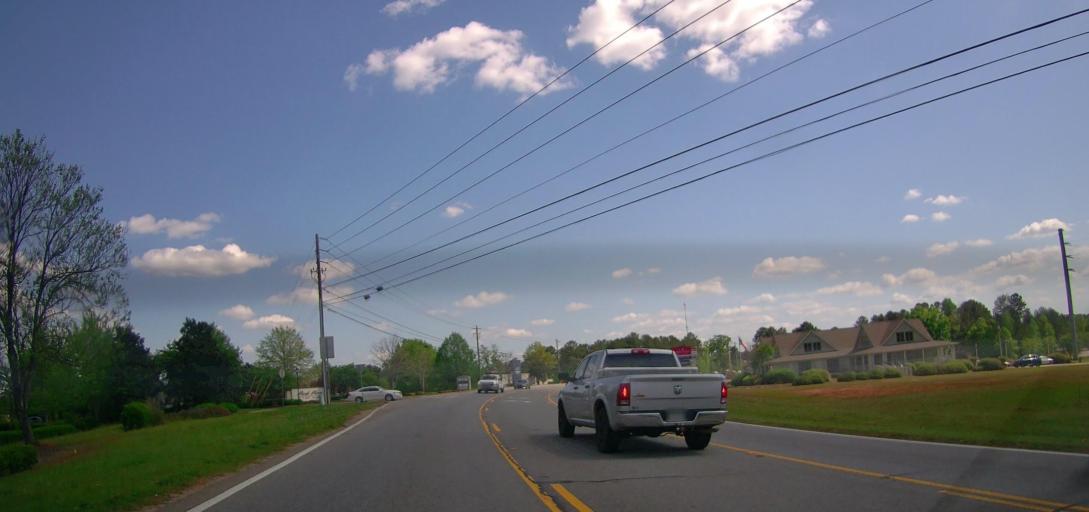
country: US
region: Georgia
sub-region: Putnam County
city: Jefferson
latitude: 33.4647
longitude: -83.2424
